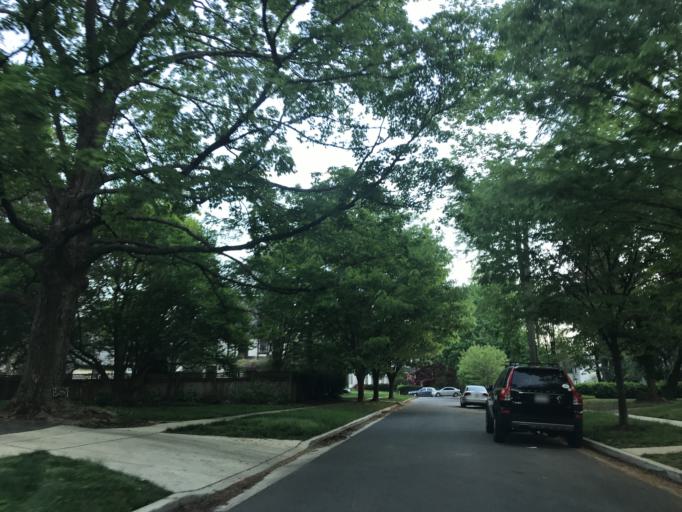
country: US
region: Maryland
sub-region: Baltimore County
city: Towson
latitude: 39.3724
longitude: -76.6171
